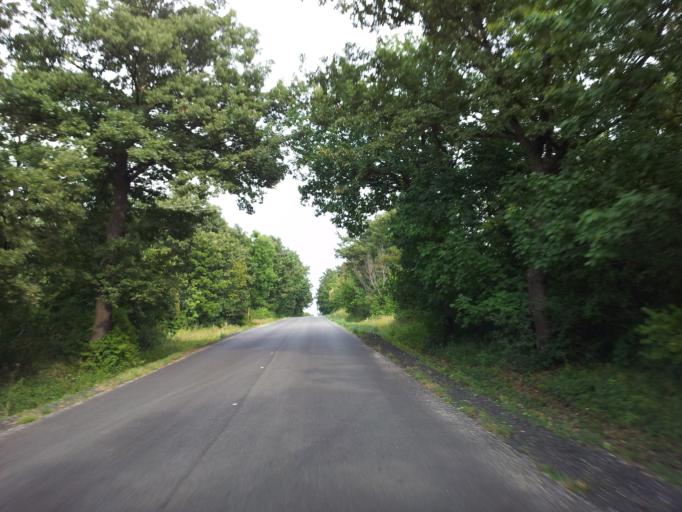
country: HU
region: Veszprem
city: Balatonfured
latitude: 46.9375
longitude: 17.8114
